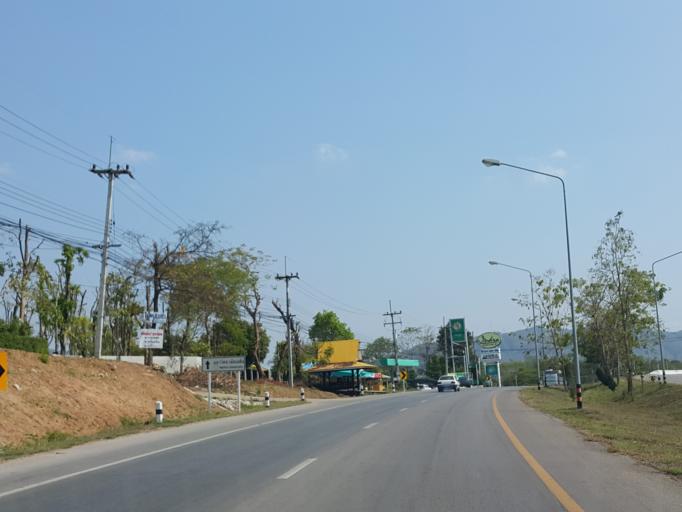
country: TH
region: Lampang
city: Lampang
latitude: 18.2828
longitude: 99.5192
